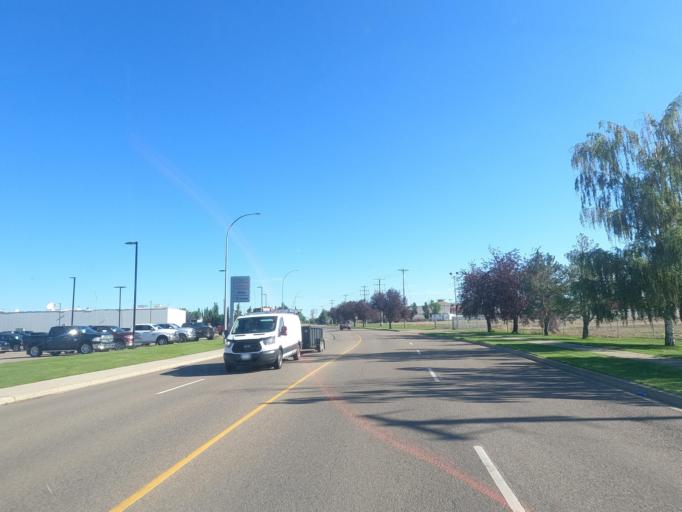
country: CA
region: Alberta
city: Brooks
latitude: 50.5759
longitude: -111.9003
